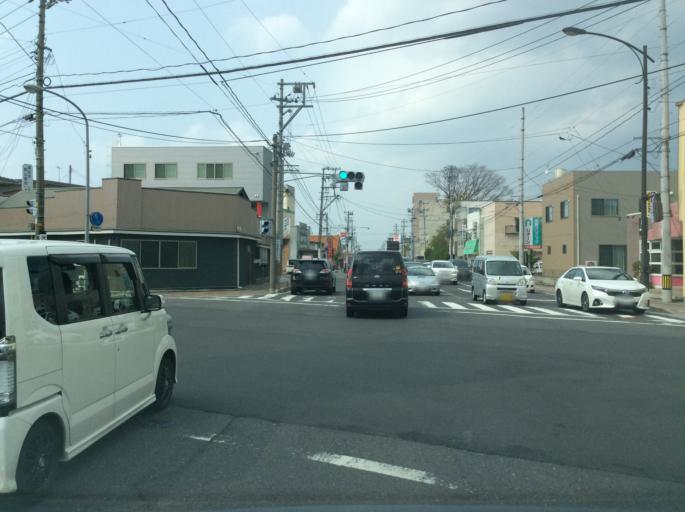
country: JP
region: Fukushima
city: Koriyama
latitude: 37.3906
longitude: 140.3943
